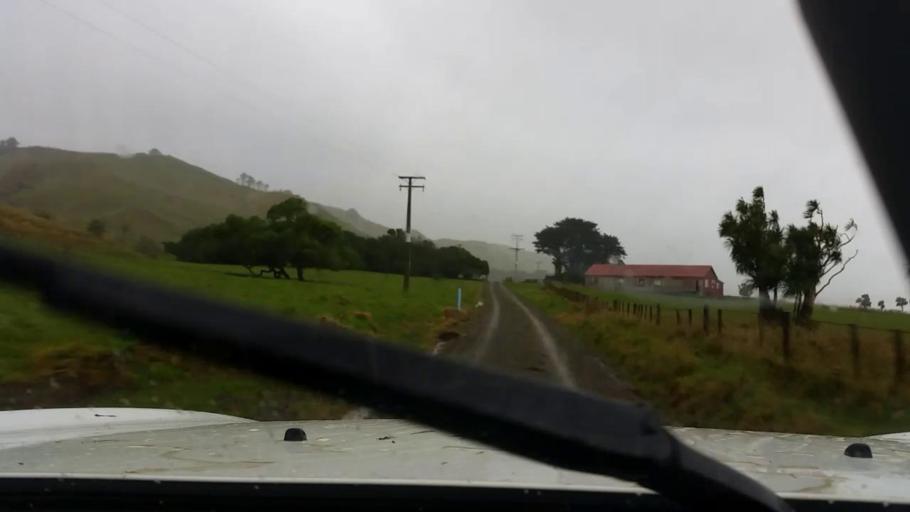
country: NZ
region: Wellington
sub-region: Masterton District
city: Masterton
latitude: -41.2632
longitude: 175.8938
